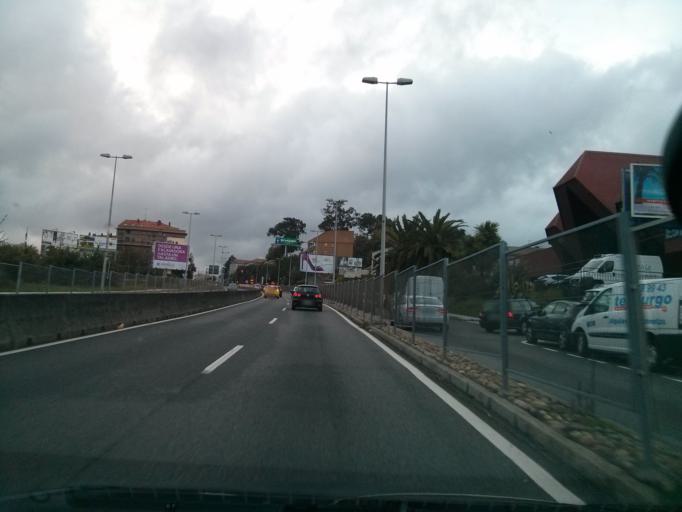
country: ES
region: Galicia
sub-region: Provincia de Pontevedra
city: Vigo
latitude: 42.2234
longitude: -8.7094
